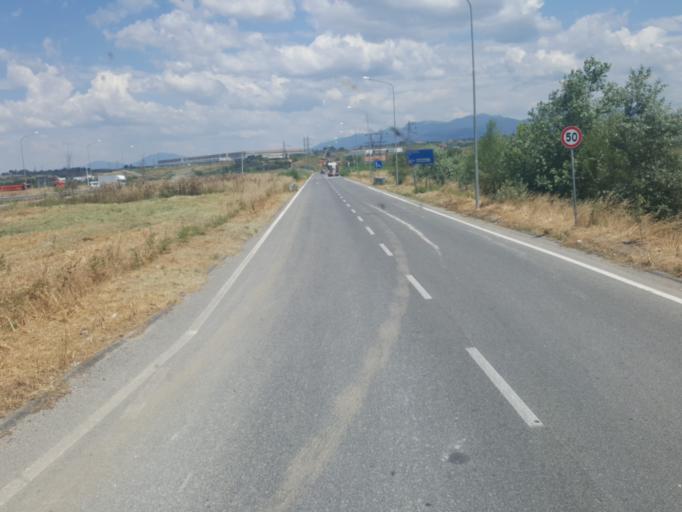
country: IT
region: Latium
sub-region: Citta metropolitana di Roma Capitale
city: Fiano Romano
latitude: 42.1554
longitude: 12.6427
